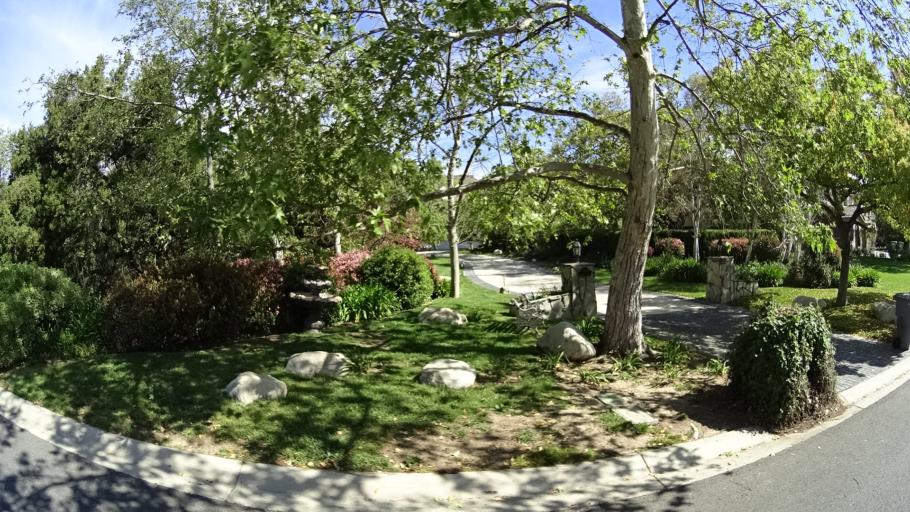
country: US
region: California
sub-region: Ventura County
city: Oak Park
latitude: 34.1858
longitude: -118.7919
